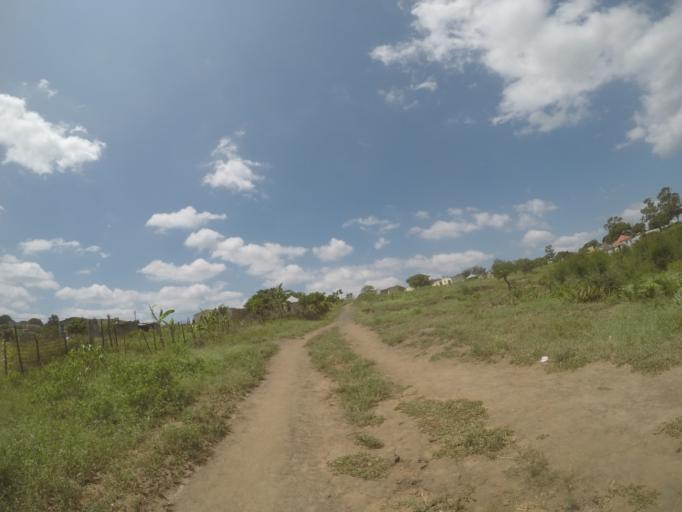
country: ZA
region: KwaZulu-Natal
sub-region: uThungulu District Municipality
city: Empangeni
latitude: -28.6027
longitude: 31.7385
